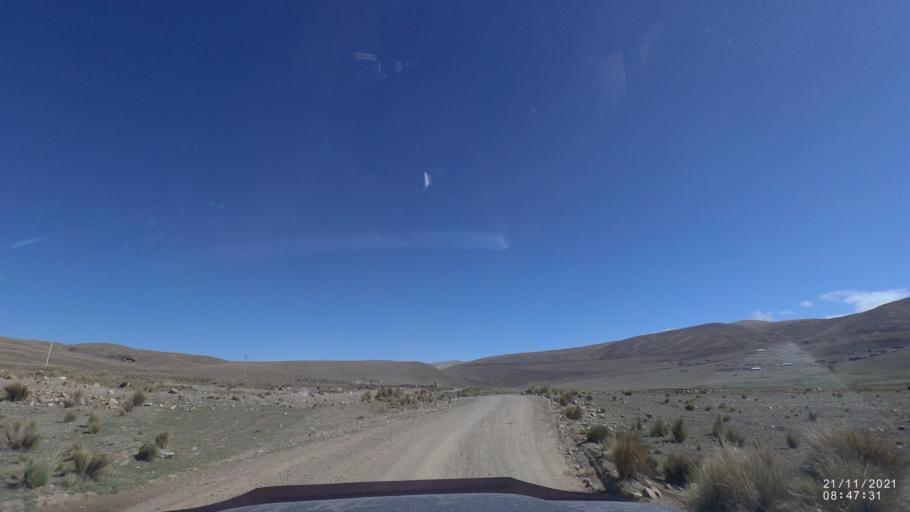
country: BO
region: Cochabamba
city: Cochabamba
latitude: -17.2349
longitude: -66.2329
